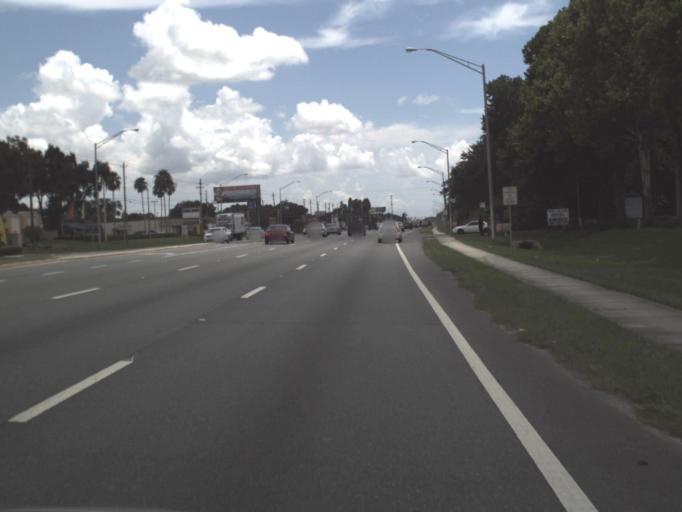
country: US
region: Florida
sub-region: Hillsborough County
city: Carrollwood
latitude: 28.0598
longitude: -82.5038
